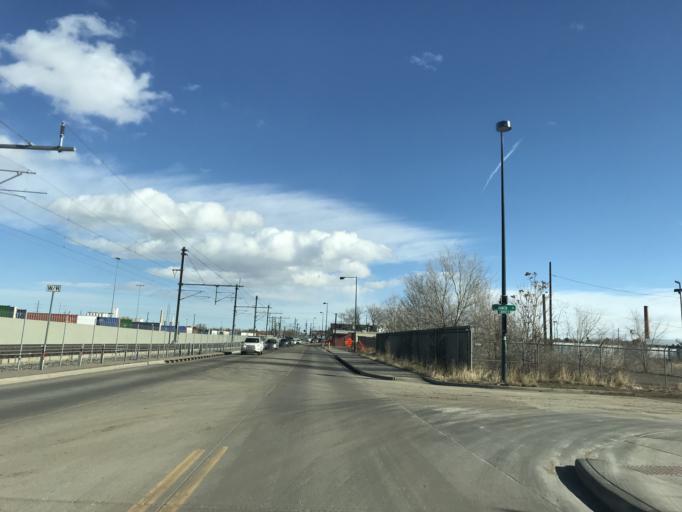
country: US
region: Colorado
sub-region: Denver County
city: Denver
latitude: 39.7729
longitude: -104.9638
